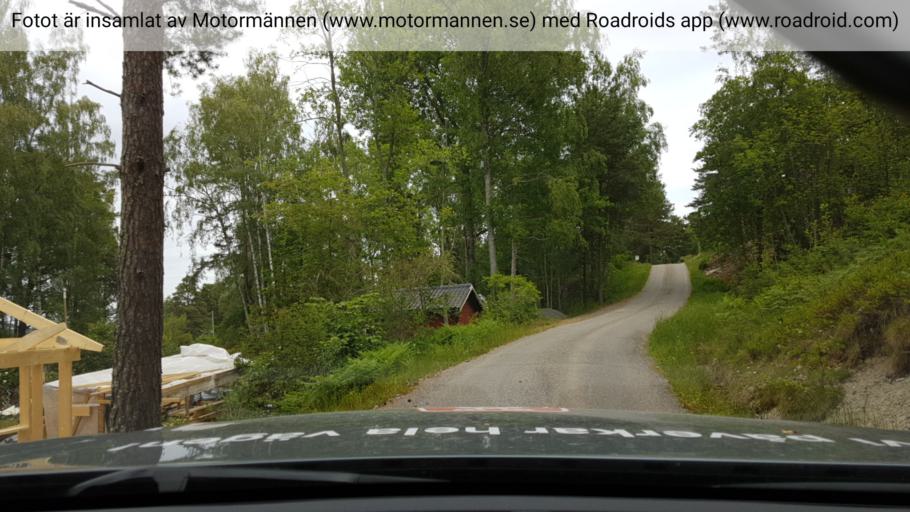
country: SE
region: Stockholm
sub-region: Haninge Kommun
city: Jordbro
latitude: 59.0195
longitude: 18.0956
